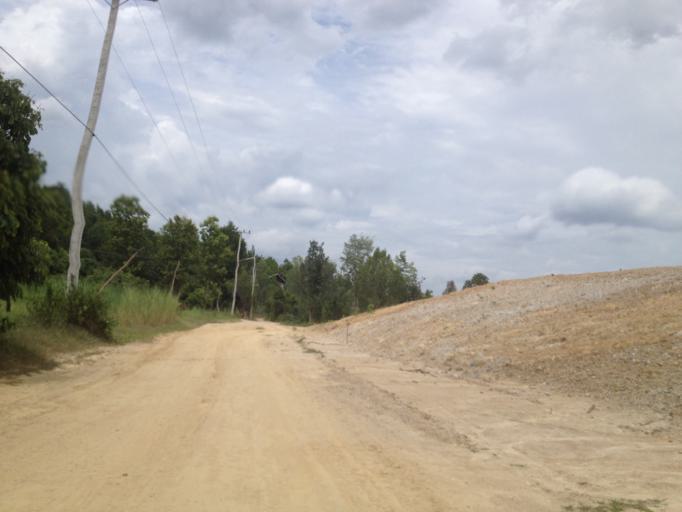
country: TH
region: Chiang Mai
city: Hang Dong
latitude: 18.6976
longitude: 98.8668
